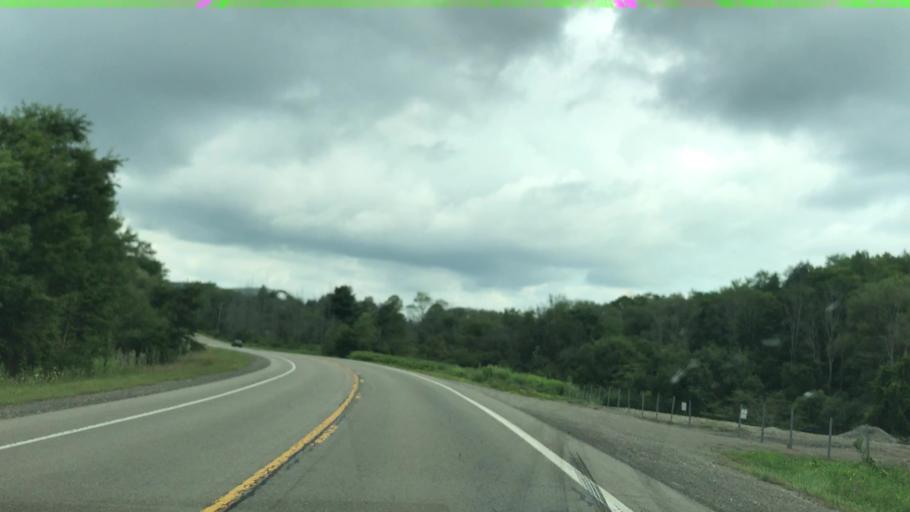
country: US
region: New York
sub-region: Steuben County
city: Bath
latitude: 42.3929
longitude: -77.3481
